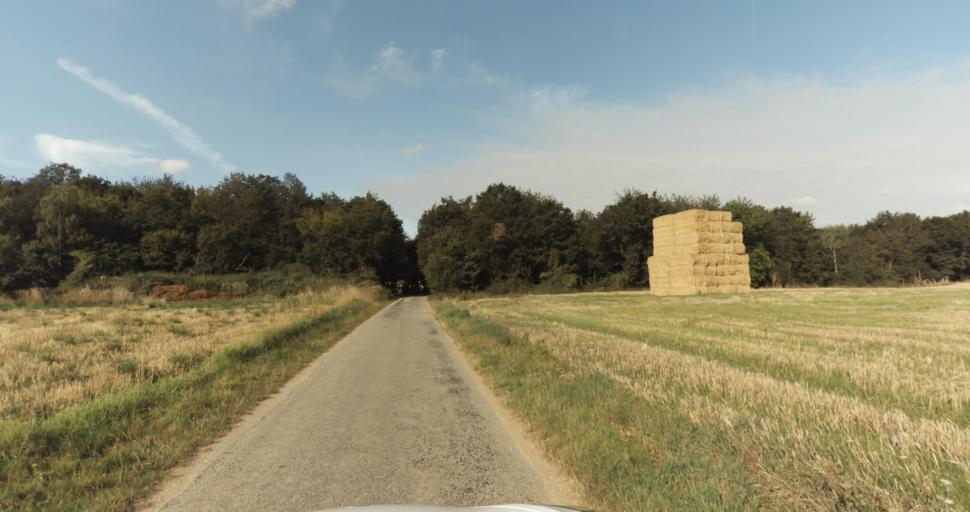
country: FR
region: Haute-Normandie
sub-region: Departement de l'Eure
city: Tillieres-sur-Avre
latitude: 48.7934
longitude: 1.0938
